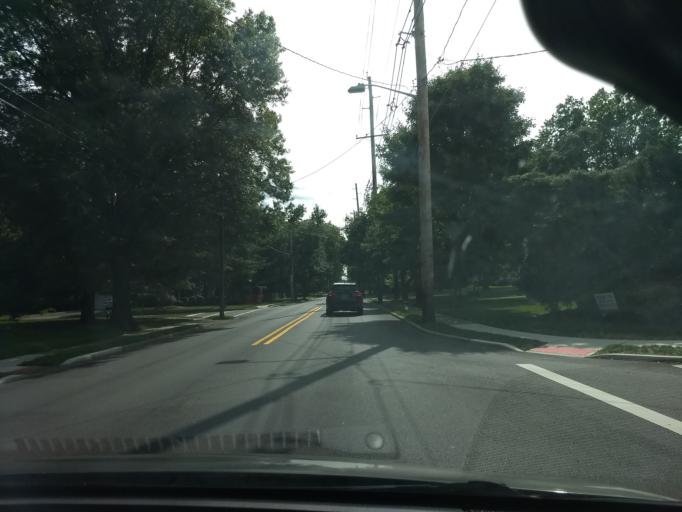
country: US
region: New Jersey
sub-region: Bergen County
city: Glen Rock
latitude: 40.9550
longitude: -74.1345
